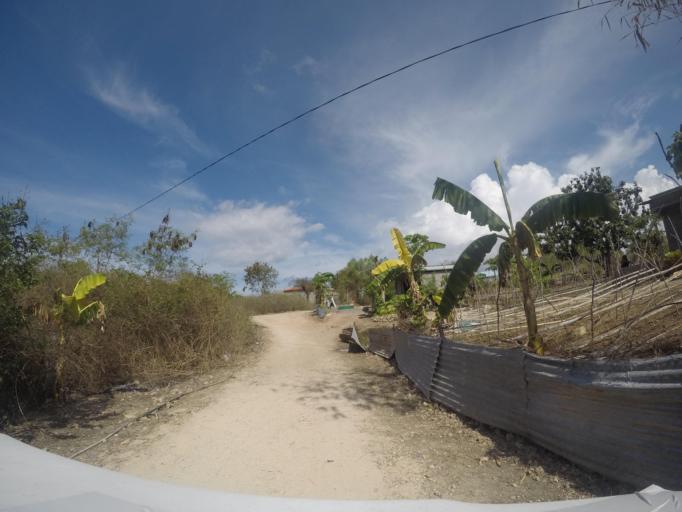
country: TL
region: Baucau
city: Baucau
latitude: -8.4637
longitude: 126.4695
